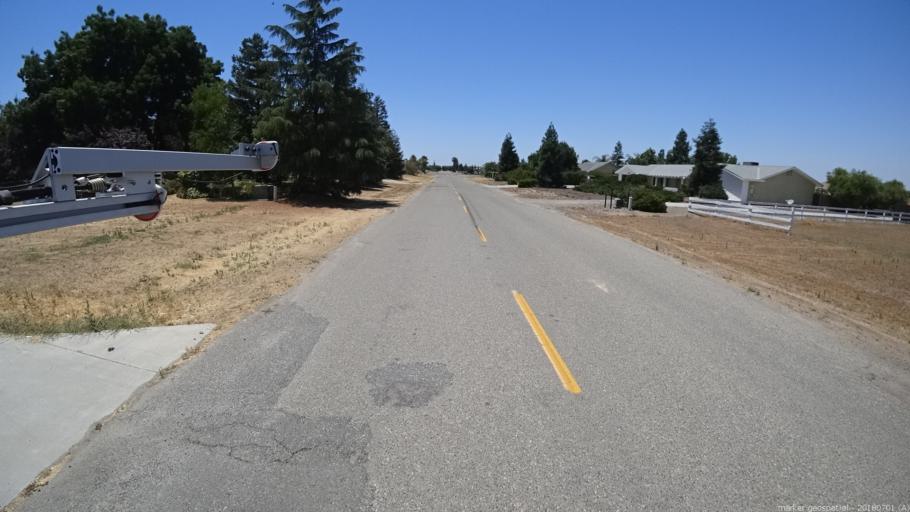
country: US
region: California
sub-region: Madera County
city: Madera Acres
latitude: 37.0558
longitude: -120.0251
